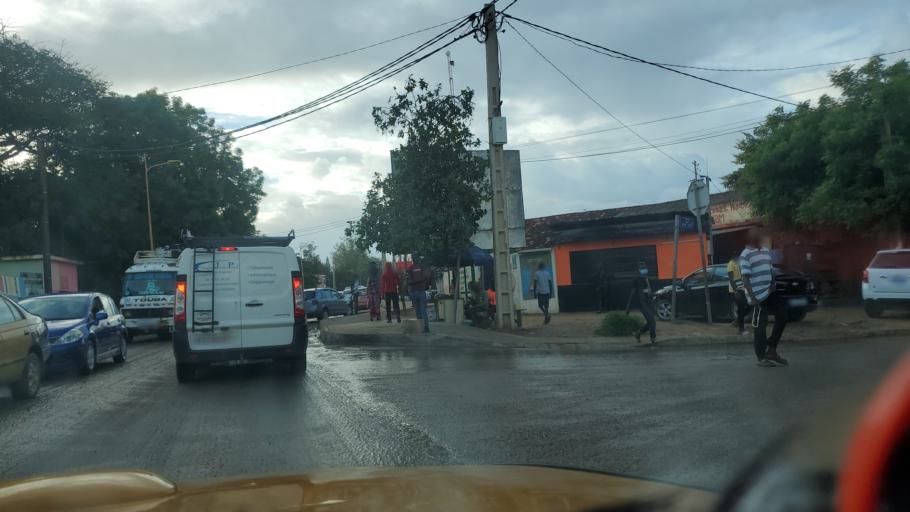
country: SN
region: Dakar
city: Mermoz Boabab
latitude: 14.7194
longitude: -17.4898
